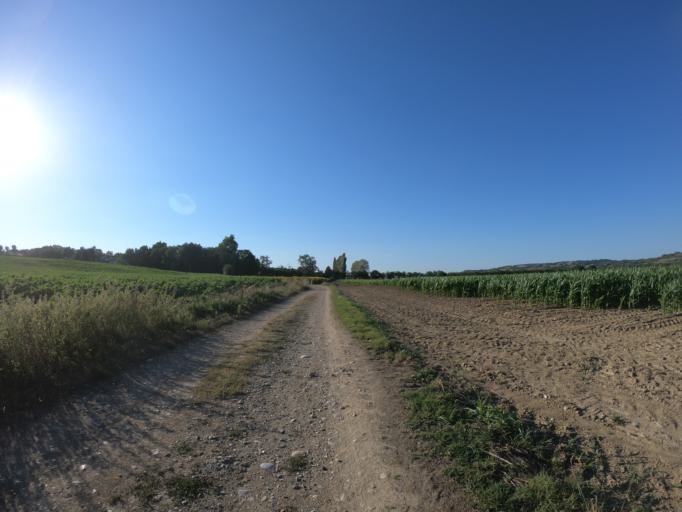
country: FR
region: Midi-Pyrenees
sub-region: Departement de l'Ariege
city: La Tour-du-Crieu
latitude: 43.1073
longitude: 1.7274
